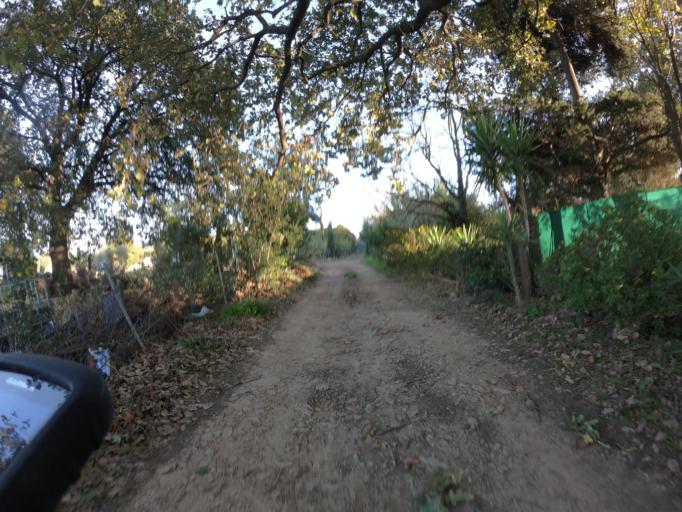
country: FR
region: Provence-Alpes-Cote d'Azur
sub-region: Departement du Var
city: Le Pradet
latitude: 43.1107
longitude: 6.0444
